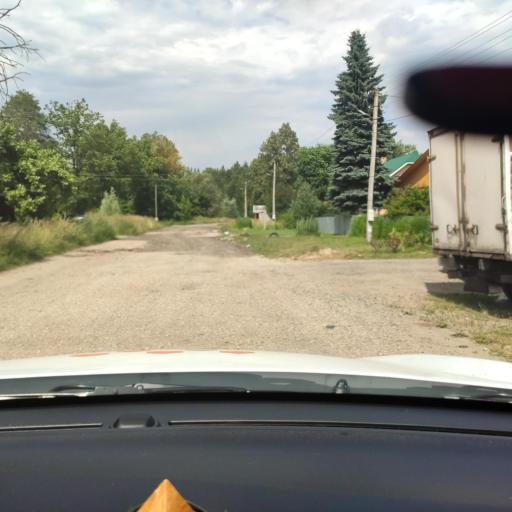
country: RU
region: Tatarstan
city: Osinovo
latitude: 55.9092
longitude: 48.9621
